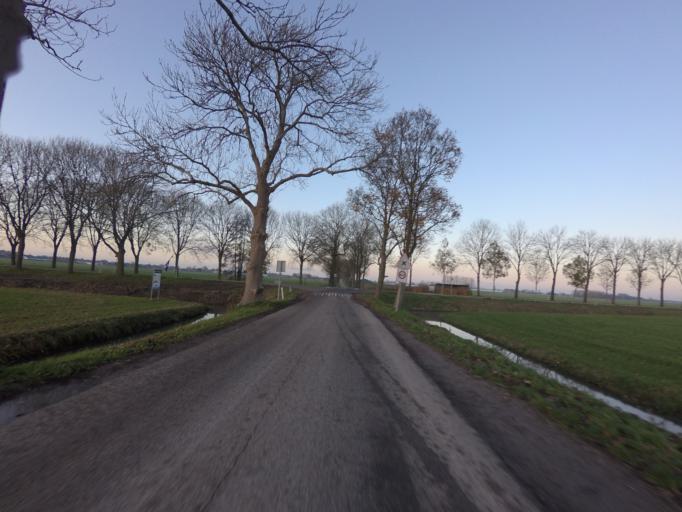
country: NL
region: Gelderland
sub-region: Gemeente Maasdriel
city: Hedel
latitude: 51.7632
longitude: 5.2253
